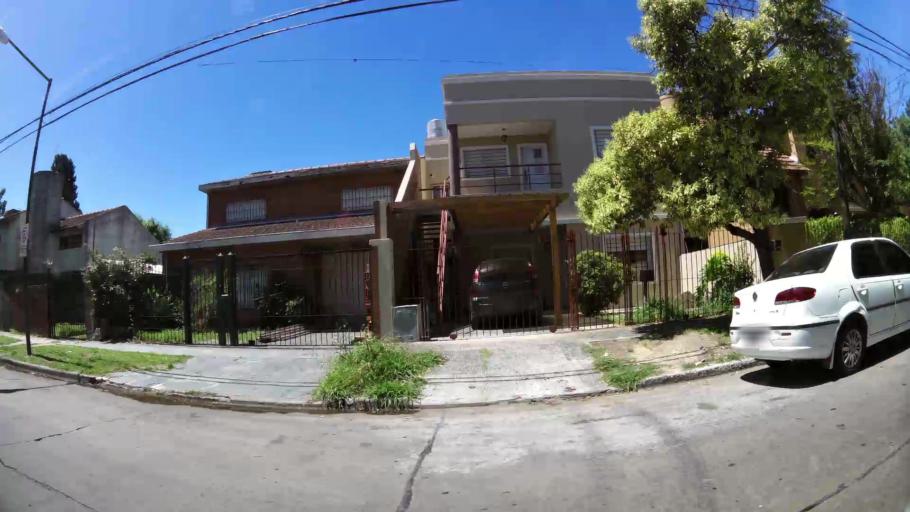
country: AR
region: Buenos Aires
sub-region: Partido de San Isidro
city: San Isidro
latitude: -34.5044
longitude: -58.5712
